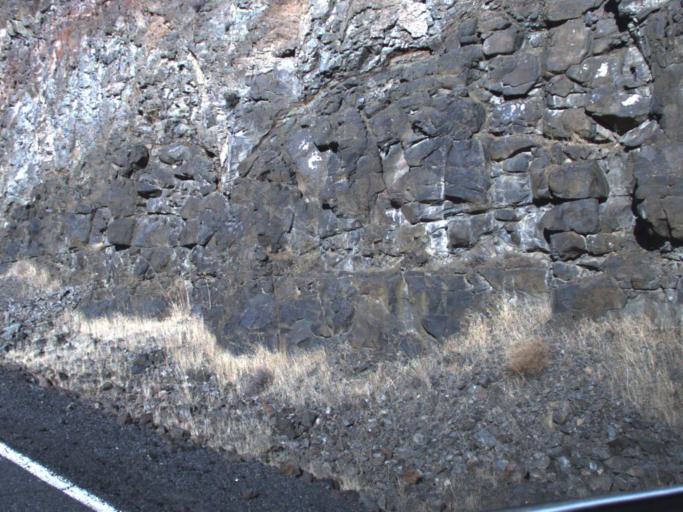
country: US
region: Washington
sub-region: Franklin County
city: Connell
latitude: 46.6263
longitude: -118.5607
